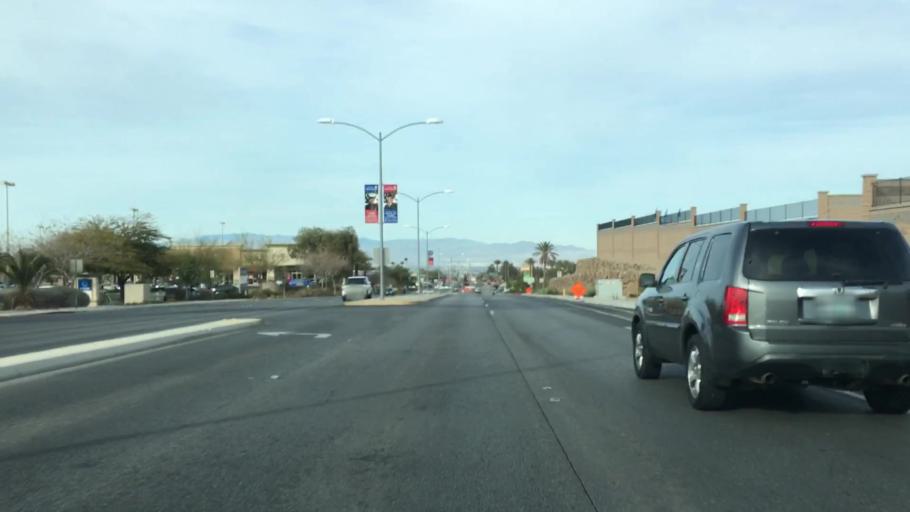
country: US
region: Nevada
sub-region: Clark County
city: Whitney
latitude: 36.0020
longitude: -115.0832
